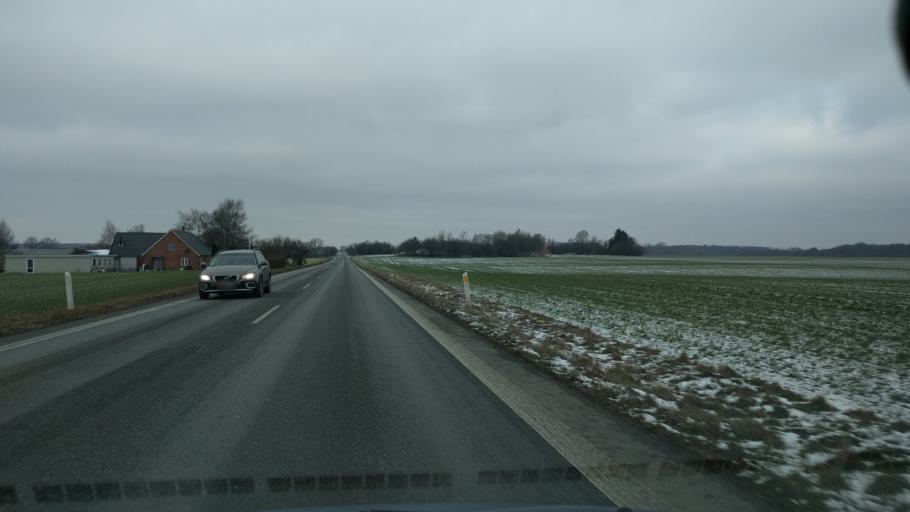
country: DK
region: Zealand
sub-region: Guldborgsund Kommune
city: Stubbekobing
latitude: 54.8147
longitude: 11.9932
